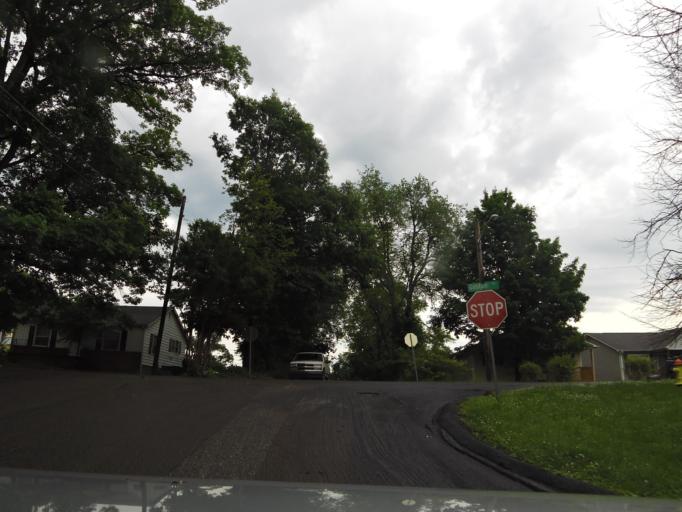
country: US
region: Tennessee
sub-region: Knox County
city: Knoxville
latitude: 36.0009
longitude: -83.9034
